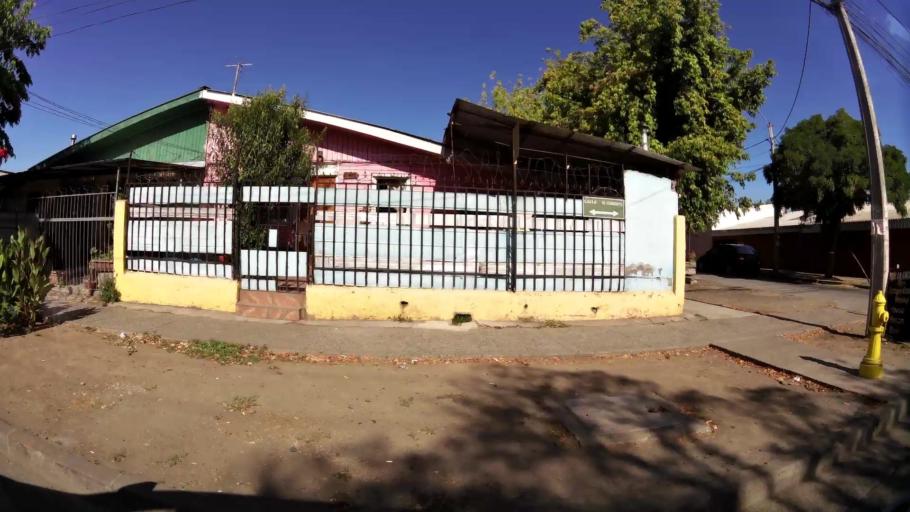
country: CL
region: Maule
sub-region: Provincia de Talca
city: Talca
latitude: -35.4419
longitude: -71.6528
